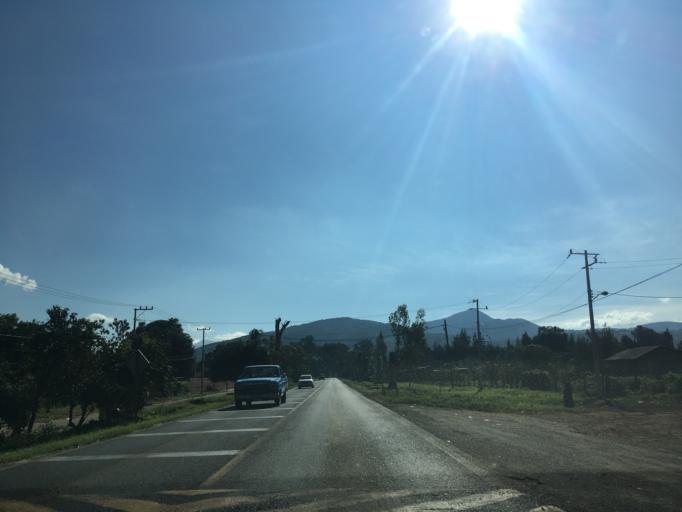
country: MX
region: Mexico
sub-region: Chalco
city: Santo Tomas
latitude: 19.8436
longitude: -102.0853
